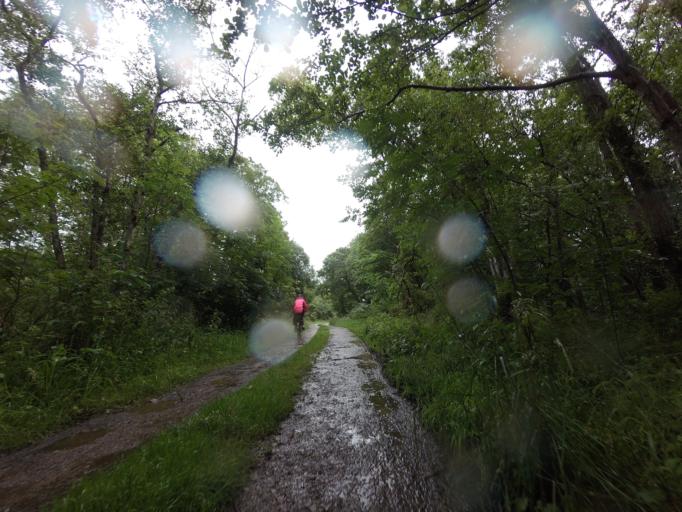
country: GB
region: Scotland
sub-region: Moray
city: Fochabers
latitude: 57.6630
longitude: -3.0929
